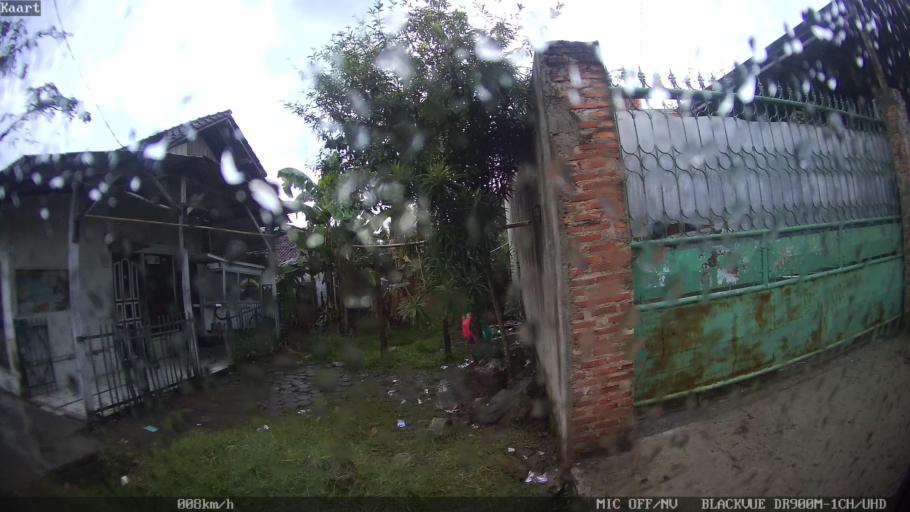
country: ID
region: Lampung
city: Kedaton
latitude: -5.3944
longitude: 105.2906
